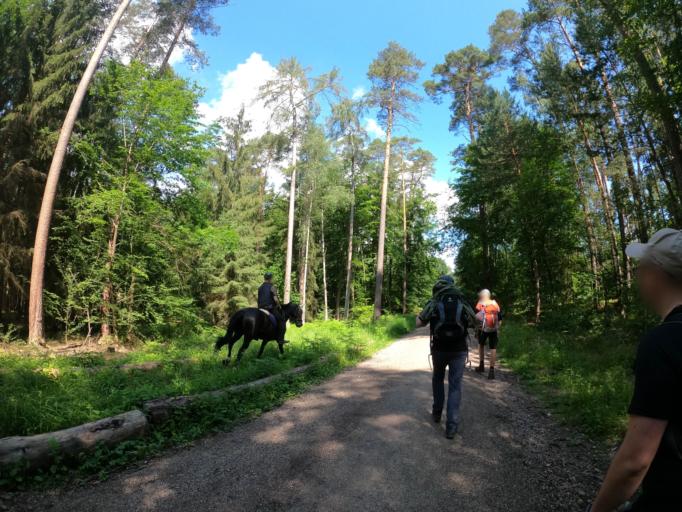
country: DE
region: Bavaria
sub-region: Upper Franconia
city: Memmelsdorf
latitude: 49.8877
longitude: 10.9551
